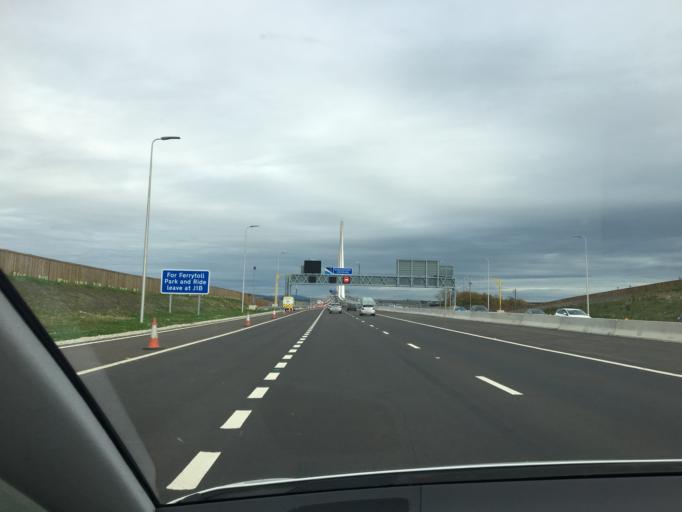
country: GB
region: Scotland
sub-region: Edinburgh
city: Queensferry
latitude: 55.9899
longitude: -3.4220
